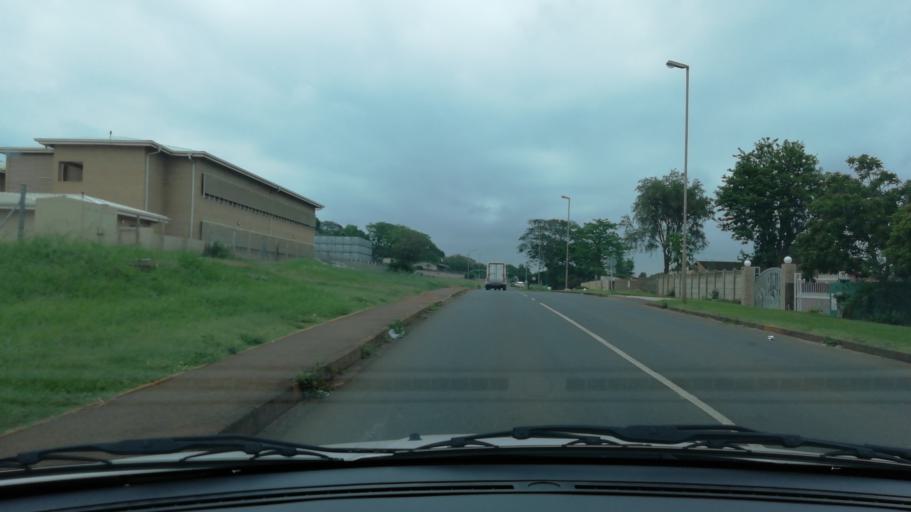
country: ZA
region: KwaZulu-Natal
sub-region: uThungulu District Municipality
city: Empangeni
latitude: -28.7394
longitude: 31.8976
